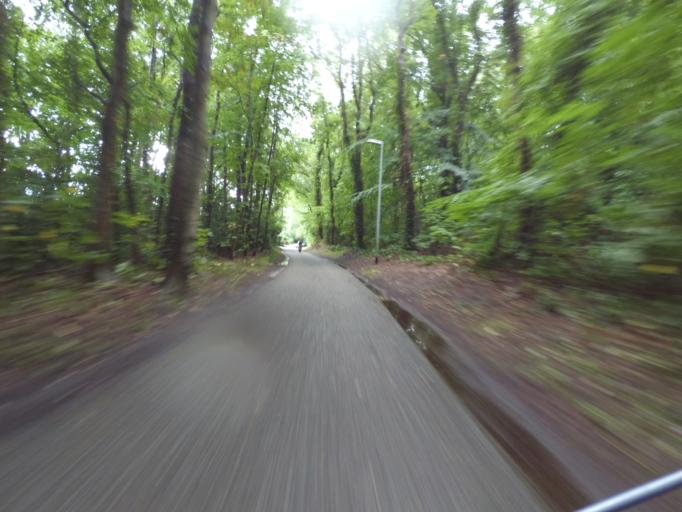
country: NL
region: North Holland
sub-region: Gemeente Alkmaar
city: Alkmaar
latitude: 52.6871
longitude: 4.6996
